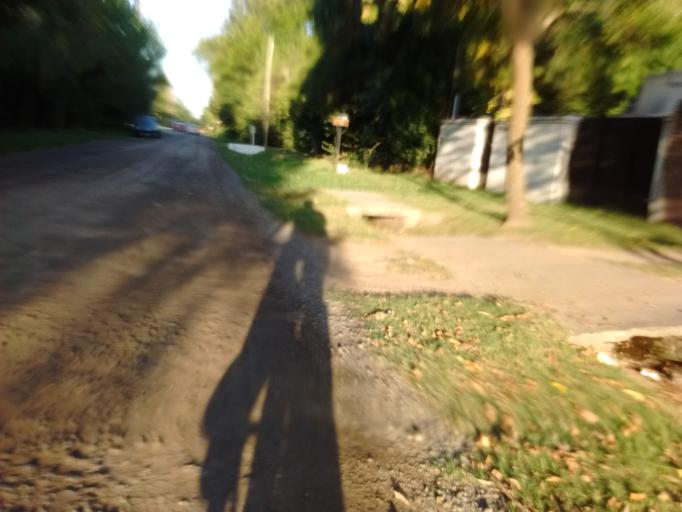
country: AR
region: Santa Fe
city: Funes
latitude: -32.9194
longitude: -60.8260
